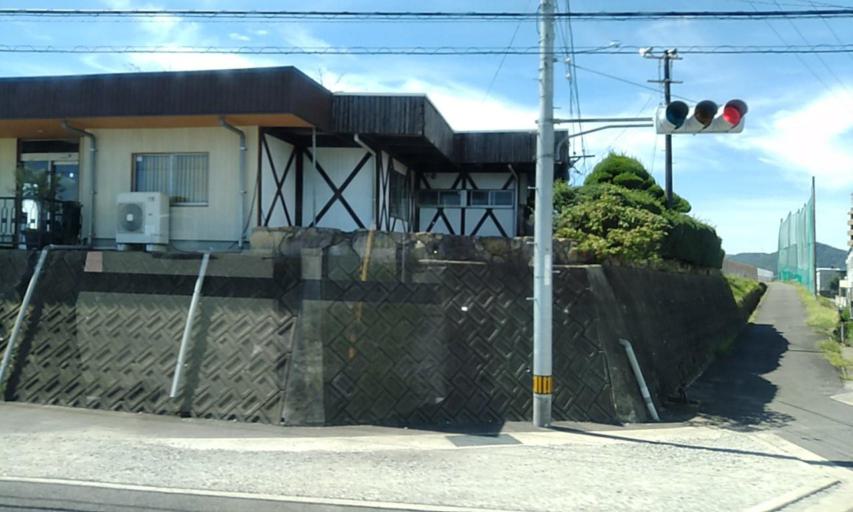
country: JP
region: Kagawa
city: Takamatsu-shi
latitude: 34.3114
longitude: 134.0708
